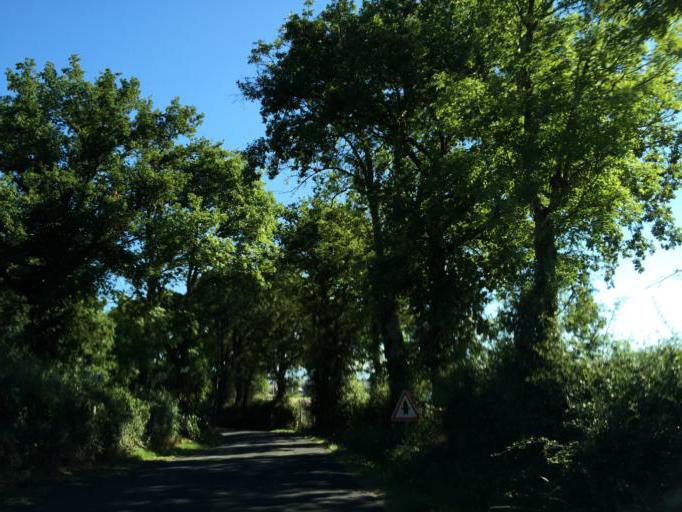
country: FR
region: Midi-Pyrenees
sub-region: Departement de l'Aveyron
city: Laissac
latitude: 44.3777
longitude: 2.8128
